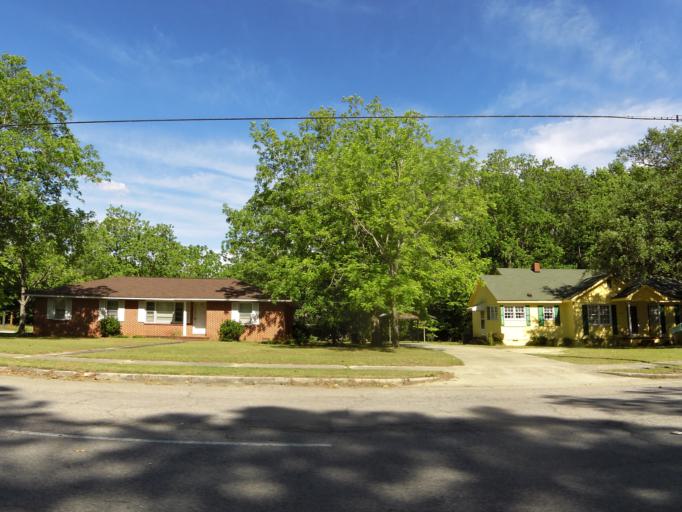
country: US
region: South Carolina
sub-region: Bamberg County
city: Denmark
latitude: 33.3113
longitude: -81.1441
